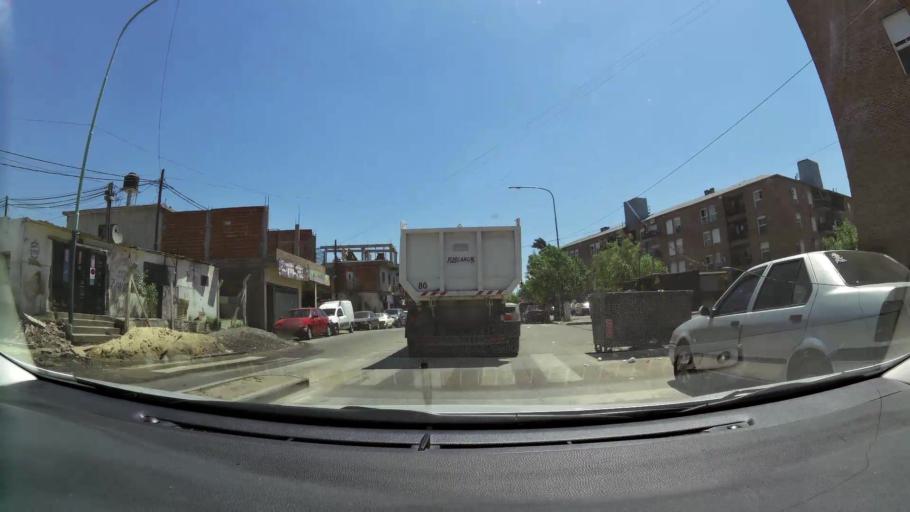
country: AR
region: Buenos Aires
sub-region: Partido de Avellaneda
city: Avellaneda
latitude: -34.6510
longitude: -58.4016
